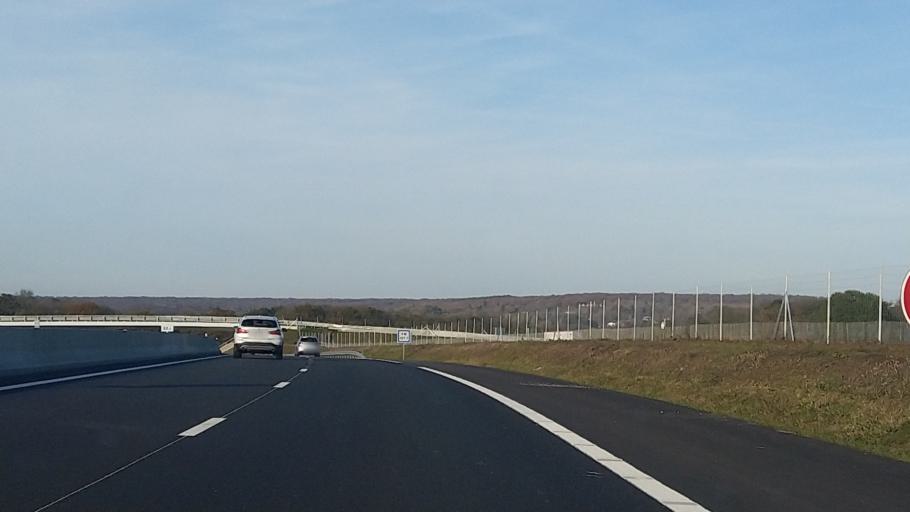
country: FR
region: Ile-de-France
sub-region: Departement du Val-d'Oise
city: Montsoult
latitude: 49.0749
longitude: 2.3326
